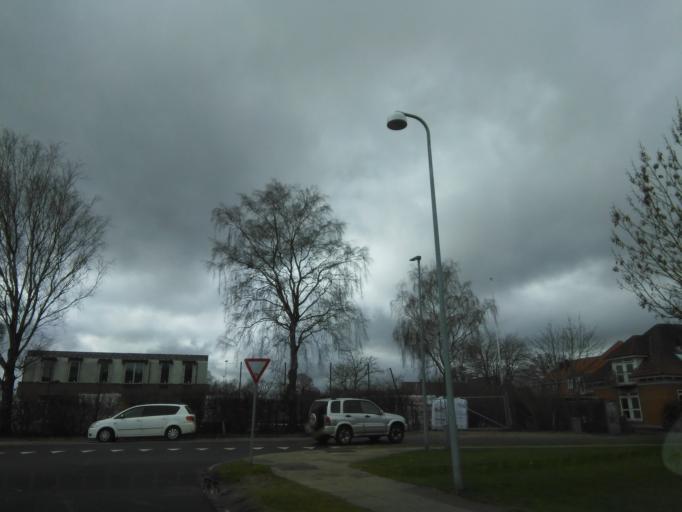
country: DK
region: Central Jutland
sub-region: Silkeborg Kommune
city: Silkeborg
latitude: 56.1599
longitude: 9.5558
